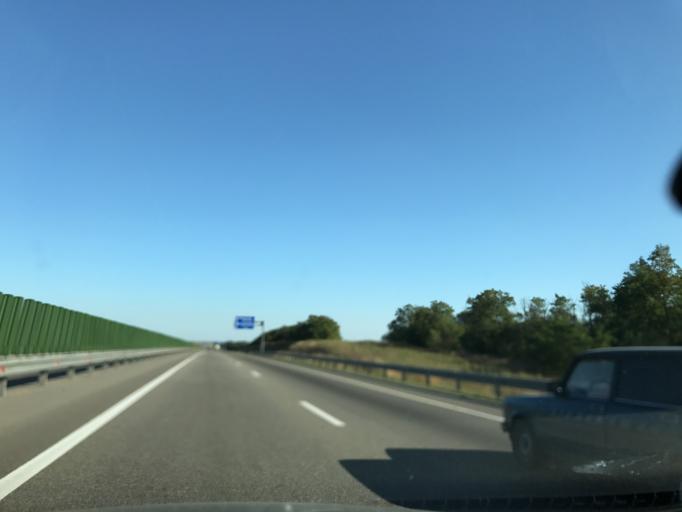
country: RU
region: Rostov
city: Glubokiy
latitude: 48.5790
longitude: 40.3521
